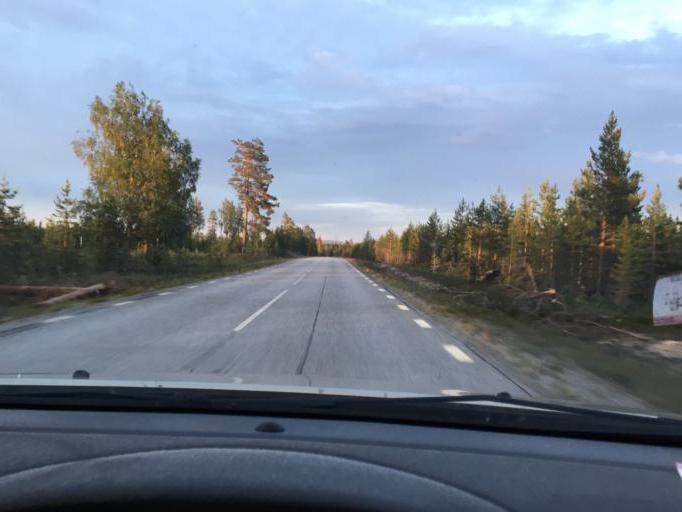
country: SE
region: Norrbotten
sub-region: Kalix Kommun
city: Toere
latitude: 66.0544
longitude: 22.4622
